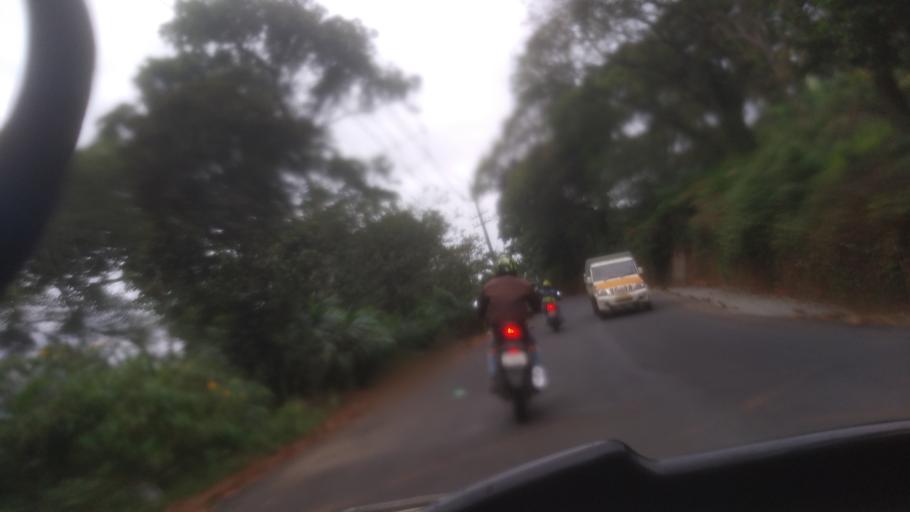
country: IN
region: Tamil Nadu
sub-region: Theni
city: Kombai
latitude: 9.8937
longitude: 77.1422
